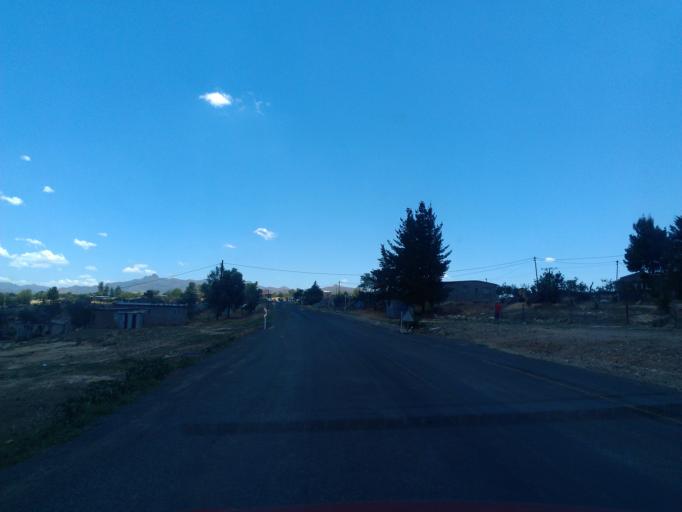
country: LS
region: Berea
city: Teyateyaneng
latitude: -29.0988
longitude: 27.9586
